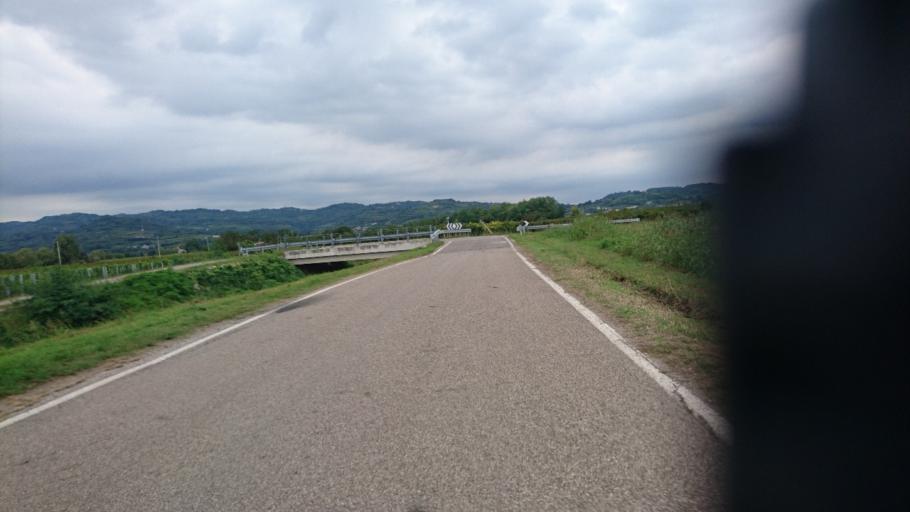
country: IT
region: Veneto
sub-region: Provincia di Vicenza
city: Gambellara
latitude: 45.4370
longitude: 11.3332
